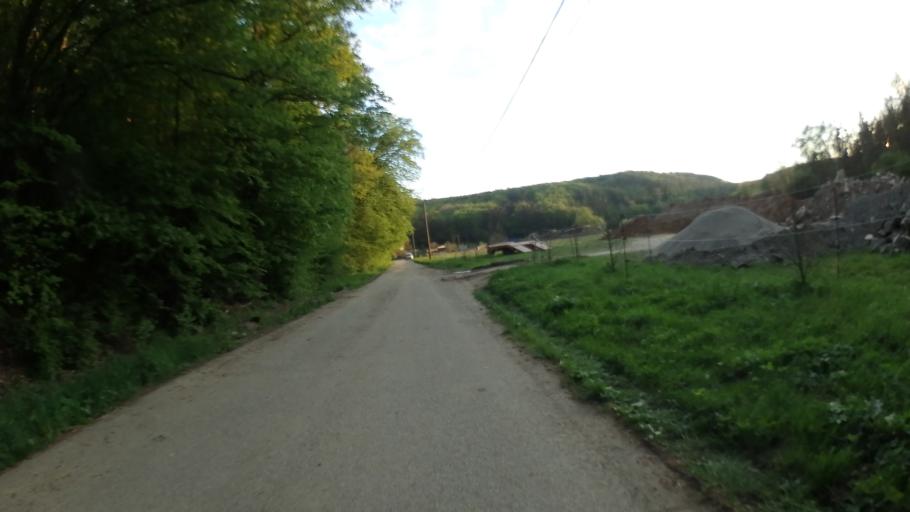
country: CZ
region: South Moravian
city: Strelice
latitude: 49.1384
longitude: 16.4772
